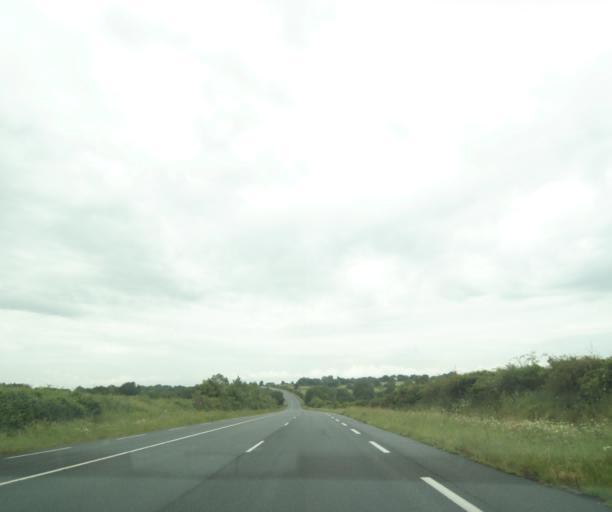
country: FR
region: Poitou-Charentes
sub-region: Departement des Deux-Sevres
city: Viennay
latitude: 46.7525
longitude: -0.2248
